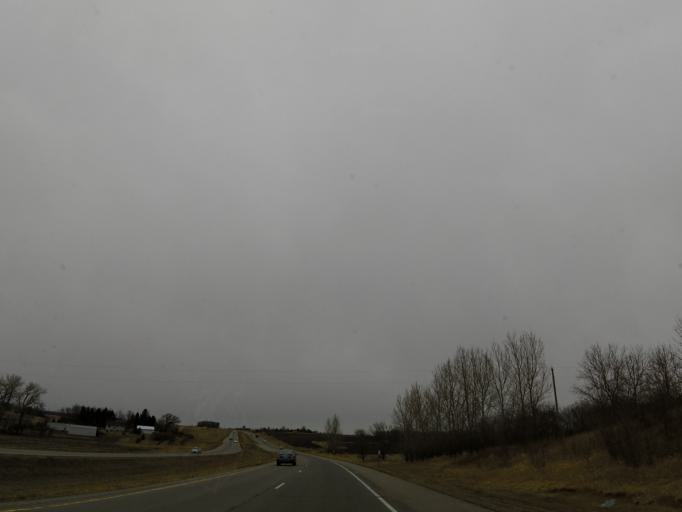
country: US
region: Minnesota
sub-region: Le Sueur County
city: Le Sueur
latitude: 44.5195
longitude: -93.8472
